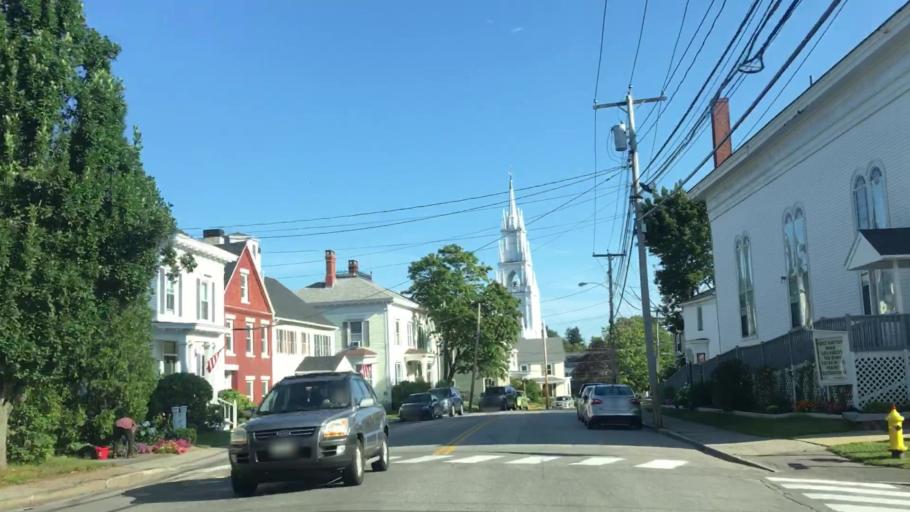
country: US
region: Maine
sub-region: Sagadahoc County
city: Bath
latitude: 43.9142
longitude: -69.8165
